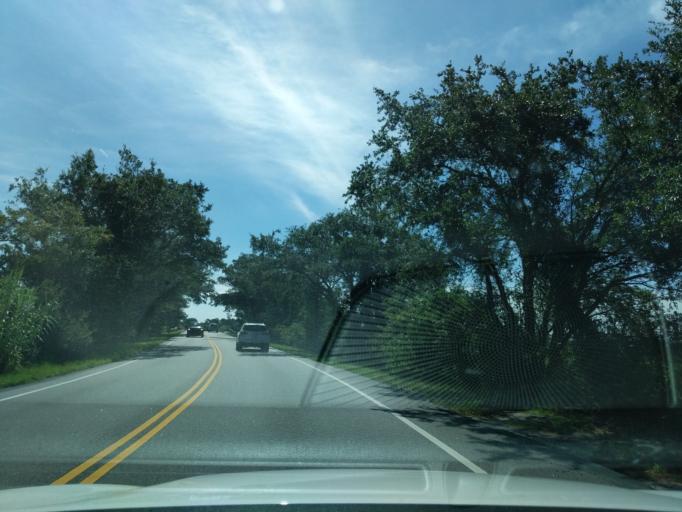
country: US
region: South Carolina
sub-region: Charleston County
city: Charleston
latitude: 32.7512
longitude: -79.9523
